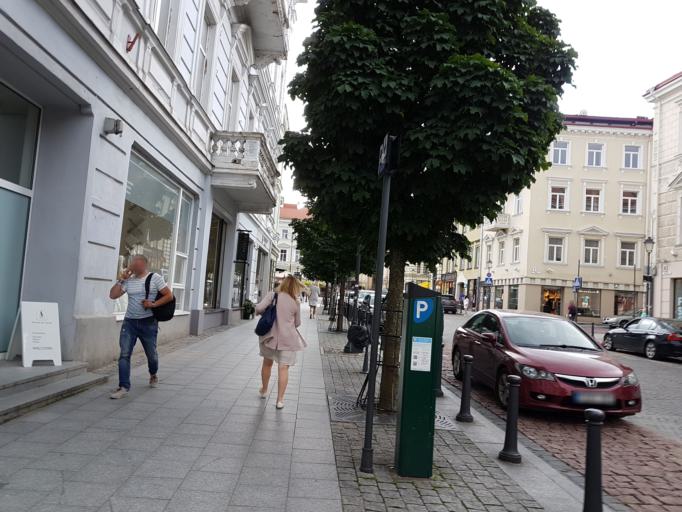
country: LT
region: Vilnius County
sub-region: Vilnius
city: Vilnius
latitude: 54.6773
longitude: 25.2880
